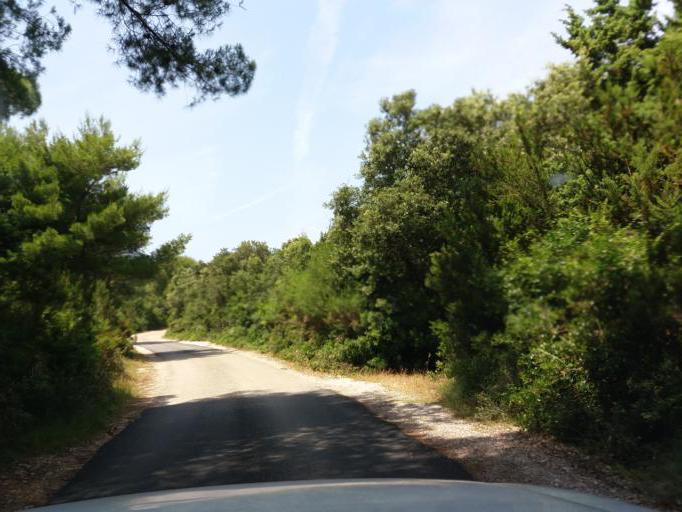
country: HR
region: Zadarska
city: Ugljan
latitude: 44.1505
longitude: 14.8247
